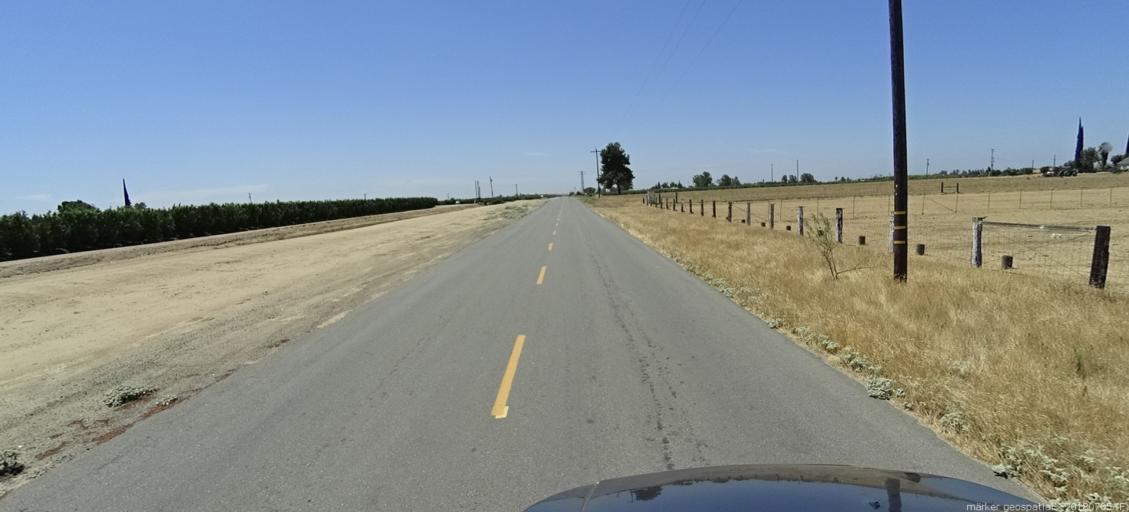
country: US
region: California
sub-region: Madera County
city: Fairmead
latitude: 37.1044
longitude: -120.2022
